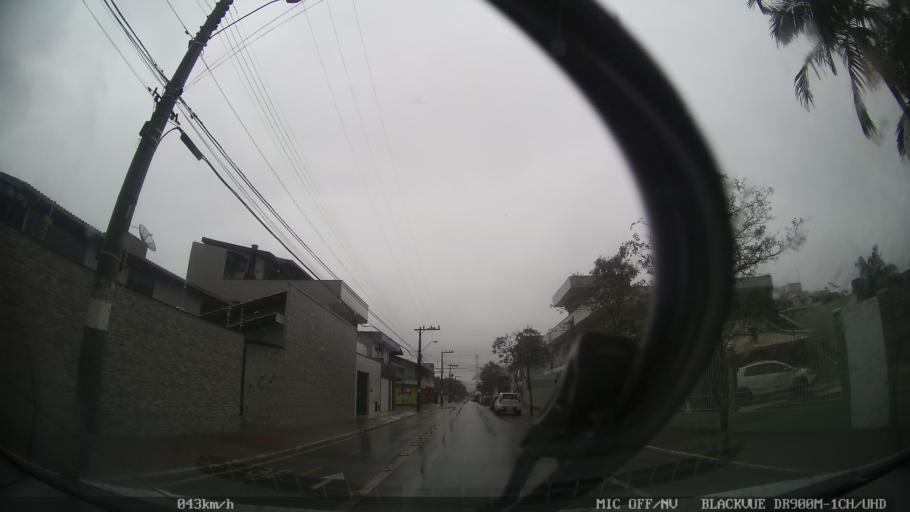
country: BR
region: Santa Catarina
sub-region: Balneario Camboriu
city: Balneario Camboriu
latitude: -27.0079
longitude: -48.6280
